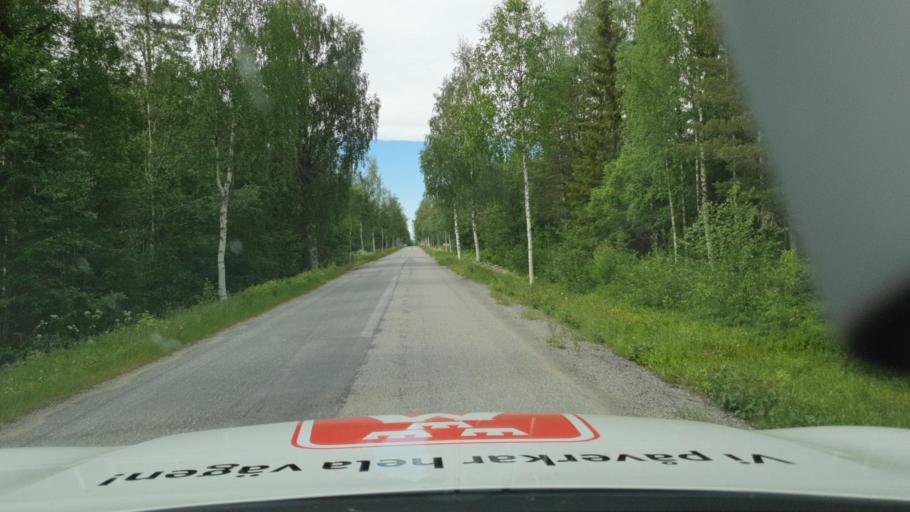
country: SE
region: Vaesterbotten
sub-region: Skelleftea Kommun
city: Burtraesk
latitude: 64.4385
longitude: 20.4984
